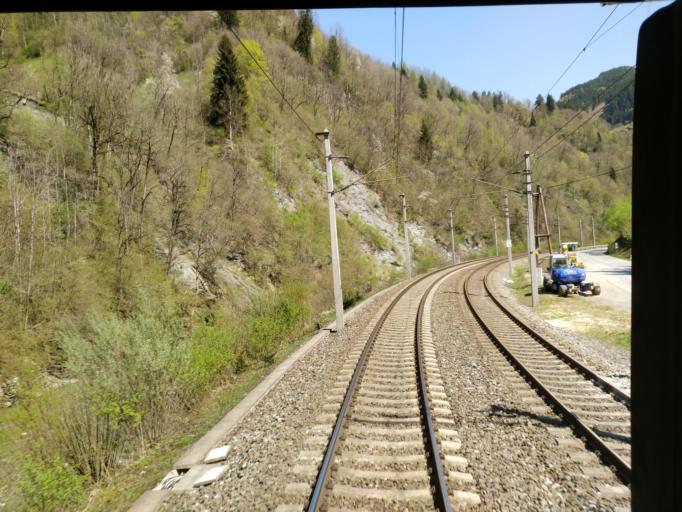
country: AT
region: Salzburg
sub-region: Politischer Bezirk Zell am See
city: Lend
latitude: 47.3076
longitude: 13.0215
